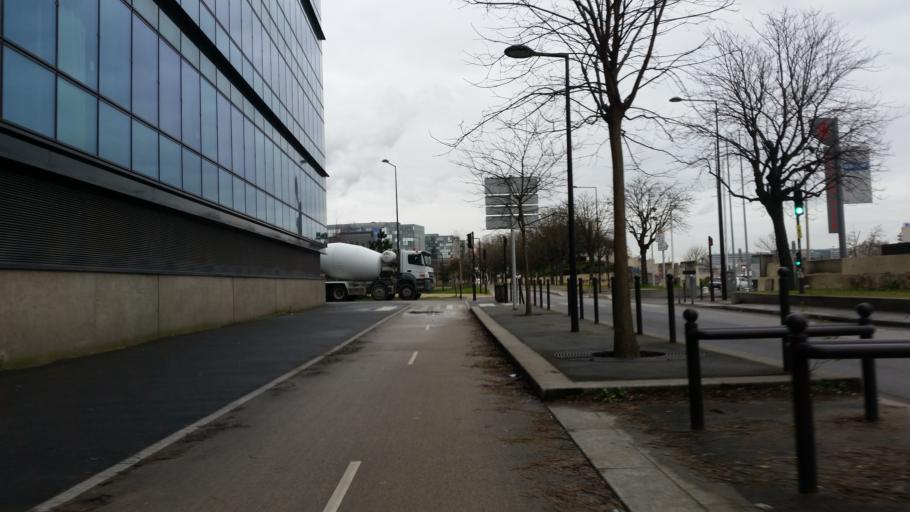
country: FR
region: Ile-de-France
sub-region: Departement du Val-de-Marne
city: Ivry-sur-Seine
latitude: 48.8204
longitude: 2.3959
